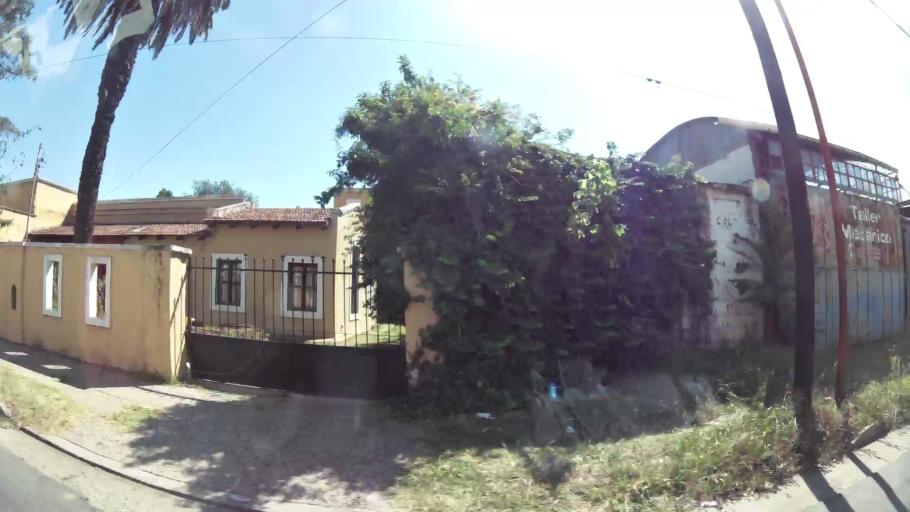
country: AR
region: Cordoba
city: Saldan
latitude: -31.2991
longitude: -64.3016
